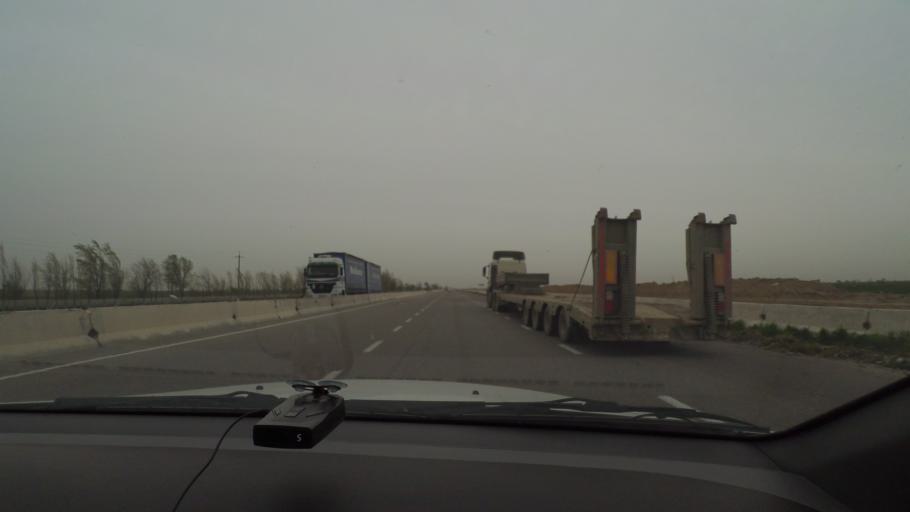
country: UZ
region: Jizzax
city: Dustlik
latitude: 40.4459
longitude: 68.2437
